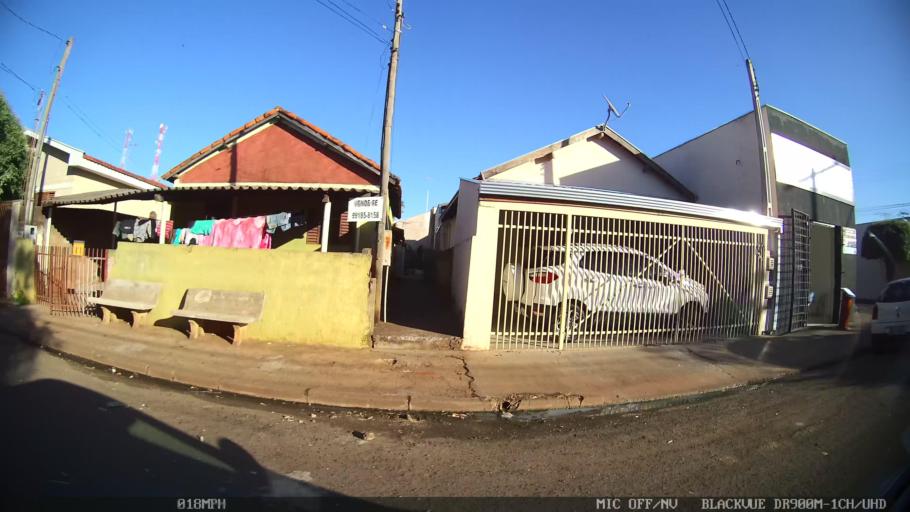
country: BR
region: Sao Paulo
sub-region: Guapiacu
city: Guapiacu
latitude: -20.7945
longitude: -49.2257
